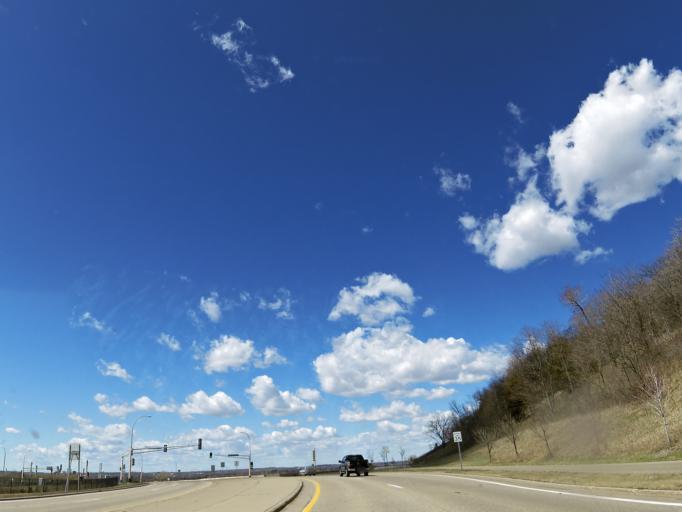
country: US
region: Minnesota
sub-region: Washington County
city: Saint Paul Park
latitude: 44.8504
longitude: -92.9870
